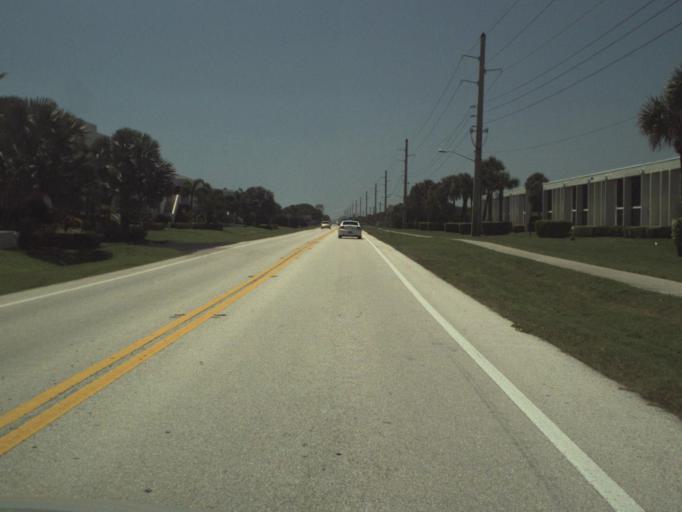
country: US
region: Florida
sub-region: Brevard County
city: Melbourne Beach
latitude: 28.0584
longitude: -80.5529
